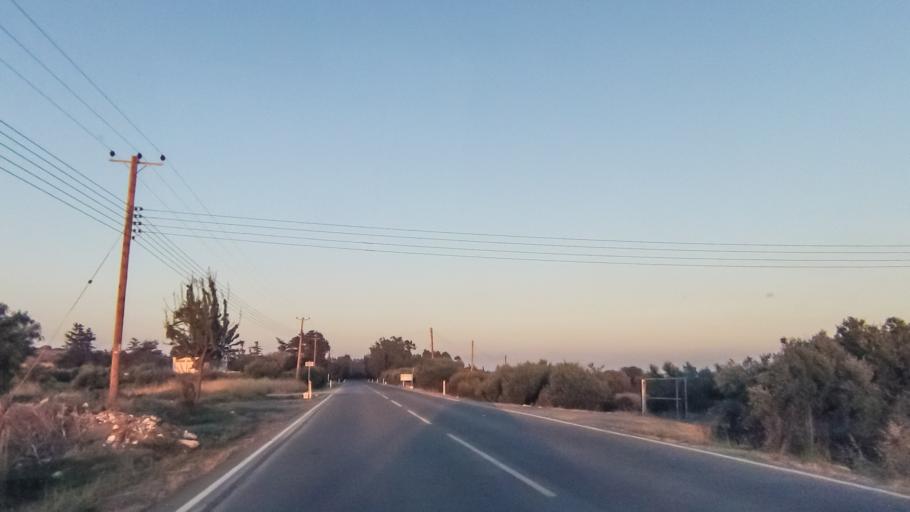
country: CY
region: Larnaka
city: Kolossi
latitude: 34.6563
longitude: 32.9216
